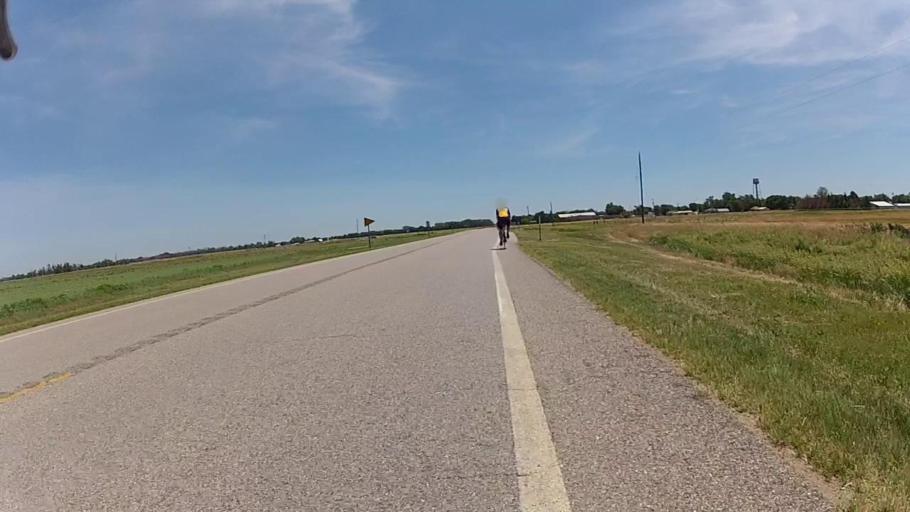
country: US
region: Kansas
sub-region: Barber County
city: Medicine Lodge
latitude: 37.2536
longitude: -98.4247
